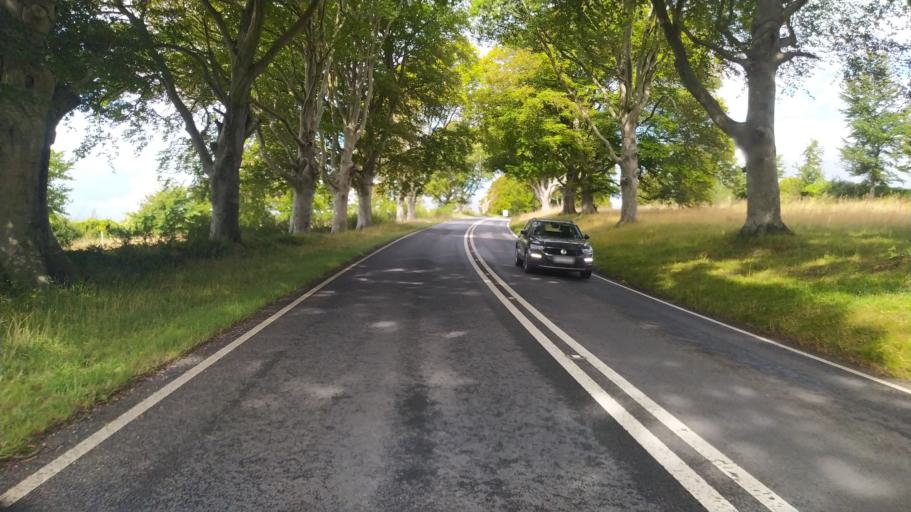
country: GB
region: England
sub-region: Dorset
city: Lytchett Matravers
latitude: 50.8200
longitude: -2.0500
